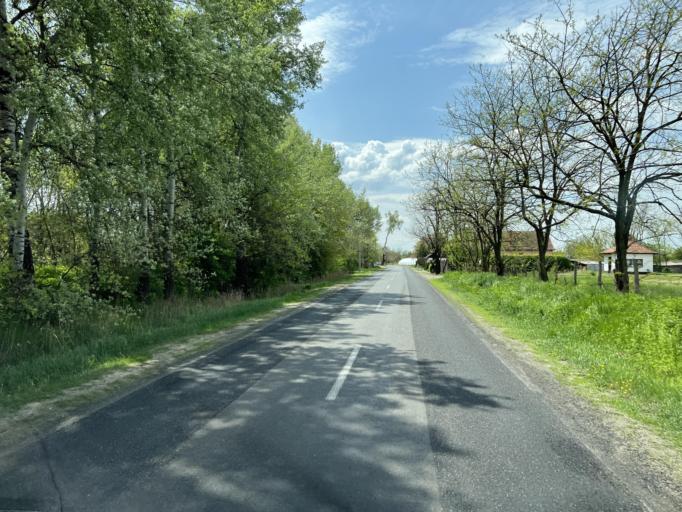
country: HU
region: Pest
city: Csemo
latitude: 47.1391
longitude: 19.7401
